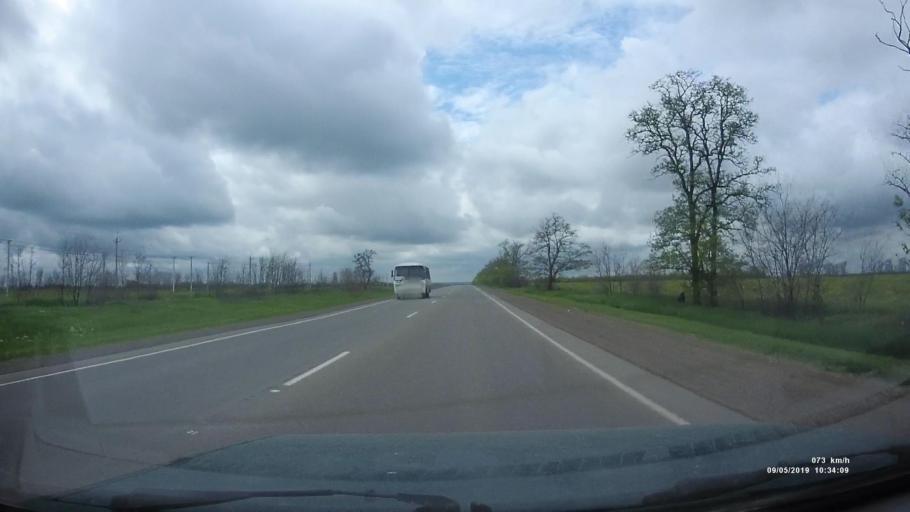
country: RU
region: Rostov
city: Azov
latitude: 47.0574
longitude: 39.4217
